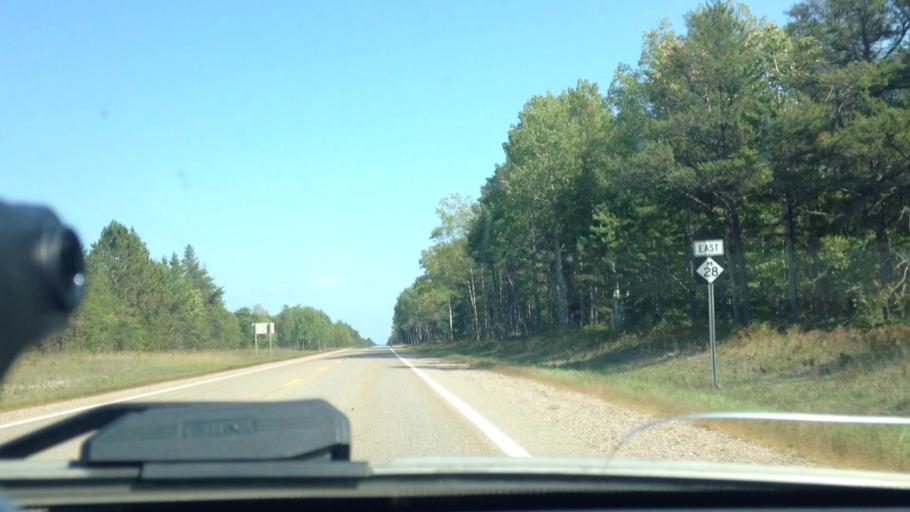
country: US
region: Michigan
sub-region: Mackinac County
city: Saint Ignace
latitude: 46.3584
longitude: -84.8623
